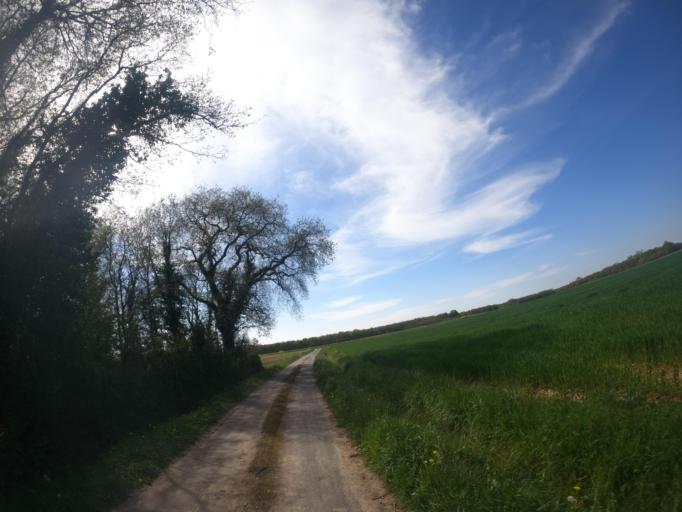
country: FR
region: Poitou-Charentes
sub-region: Departement des Deux-Sevres
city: Saint-Varent
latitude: 46.9255
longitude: -0.2306
